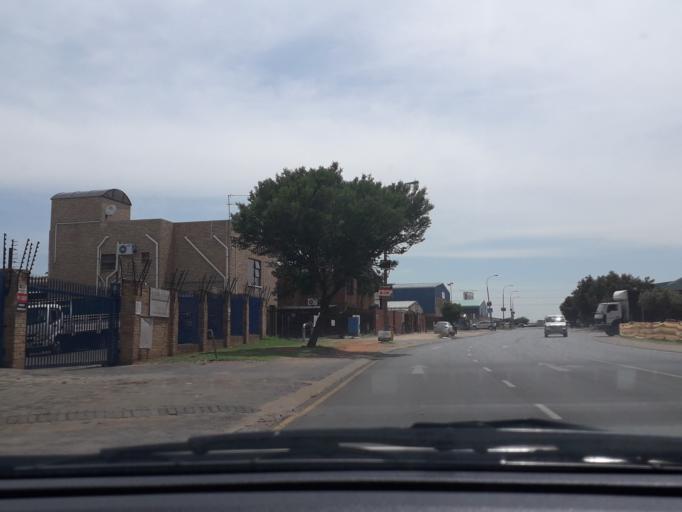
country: ZA
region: Gauteng
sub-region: City of Johannesburg Metropolitan Municipality
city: Roodepoort
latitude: -26.1953
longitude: 27.9220
